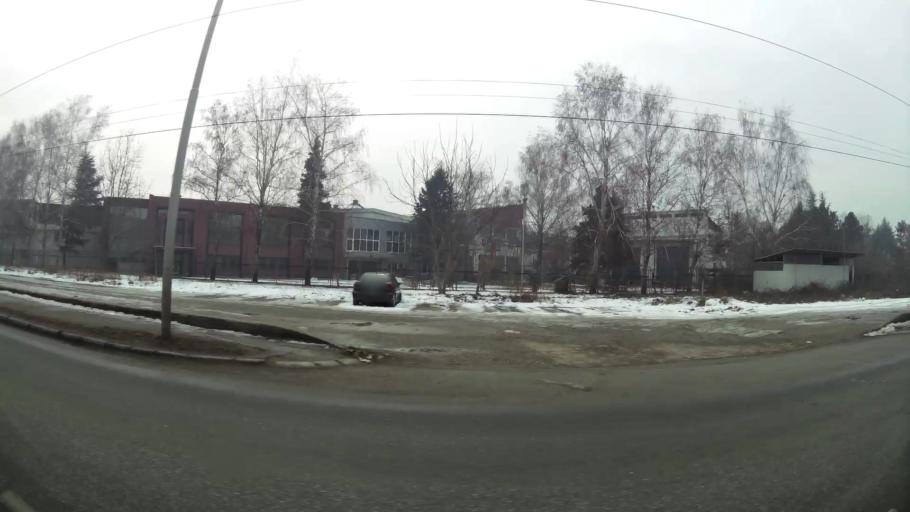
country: MK
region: Kisela Voda
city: Usje
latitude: 41.9971
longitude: 21.4853
